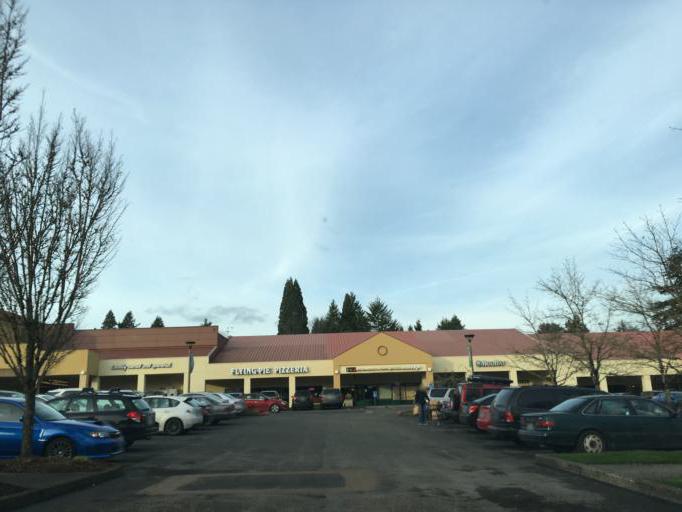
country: US
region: Oregon
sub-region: Clackamas County
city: Lake Oswego
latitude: 45.4331
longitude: -122.7029
